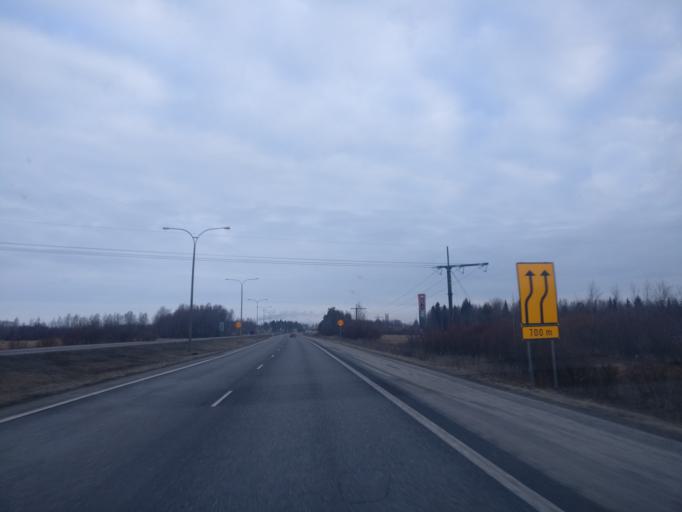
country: FI
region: Northern Ostrobothnia
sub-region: Oulu
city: Kempele
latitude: 64.9521
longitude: 25.5269
